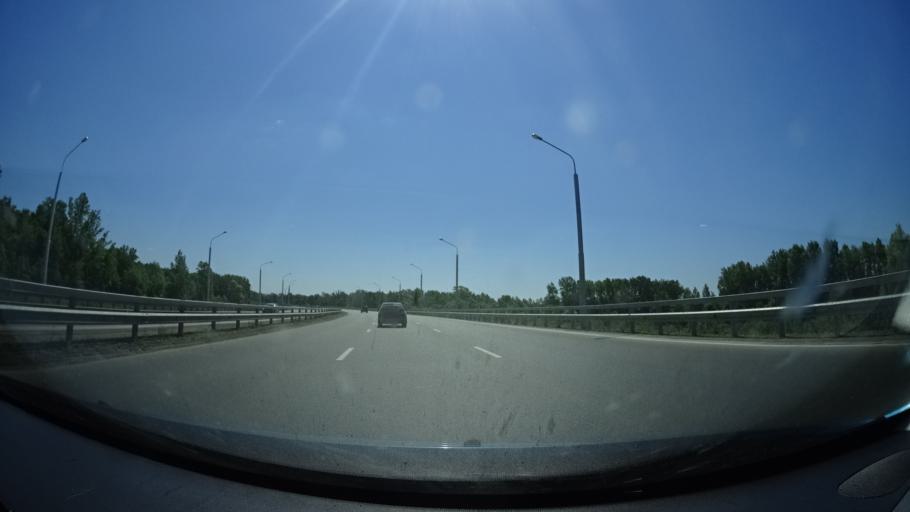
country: RU
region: Bashkortostan
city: Mikhaylovka
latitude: 54.7838
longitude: 55.9107
